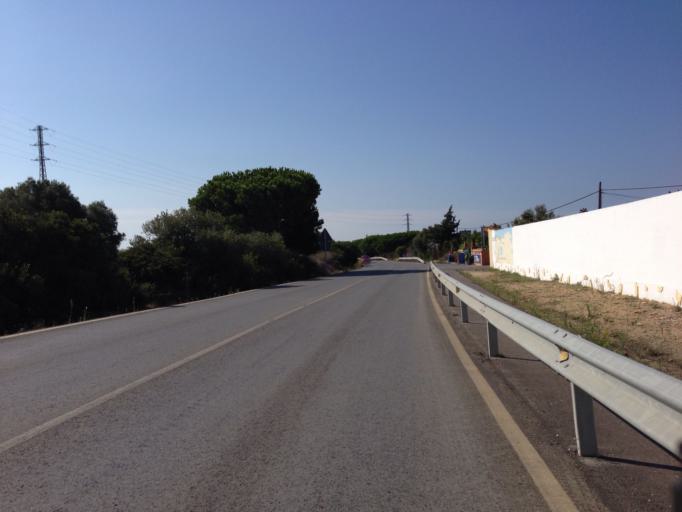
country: ES
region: Andalusia
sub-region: Provincia de Cadiz
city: Vejer de la Frontera
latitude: 36.1971
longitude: -6.0306
